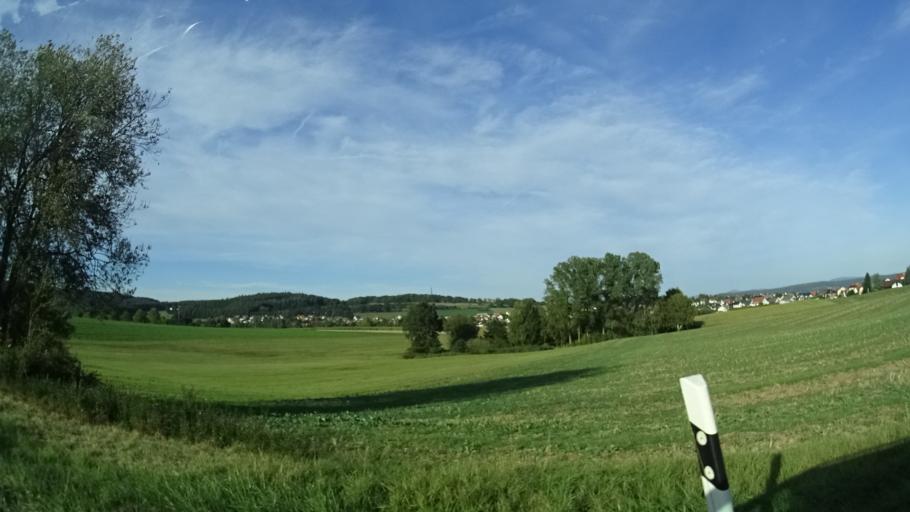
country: DE
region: Hesse
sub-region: Regierungsbezirk Kassel
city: Flieden
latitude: 50.4208
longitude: 9.5517
